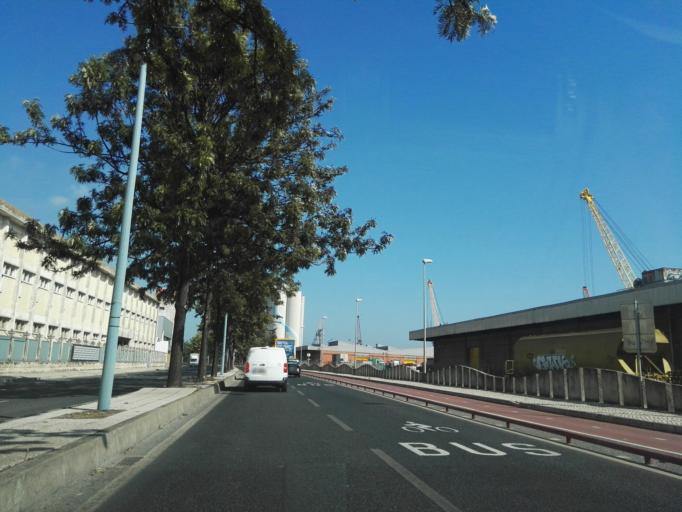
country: PT
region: Lisbon
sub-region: Lisbon
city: Lisbon
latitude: 38.7307
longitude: -9.1056
